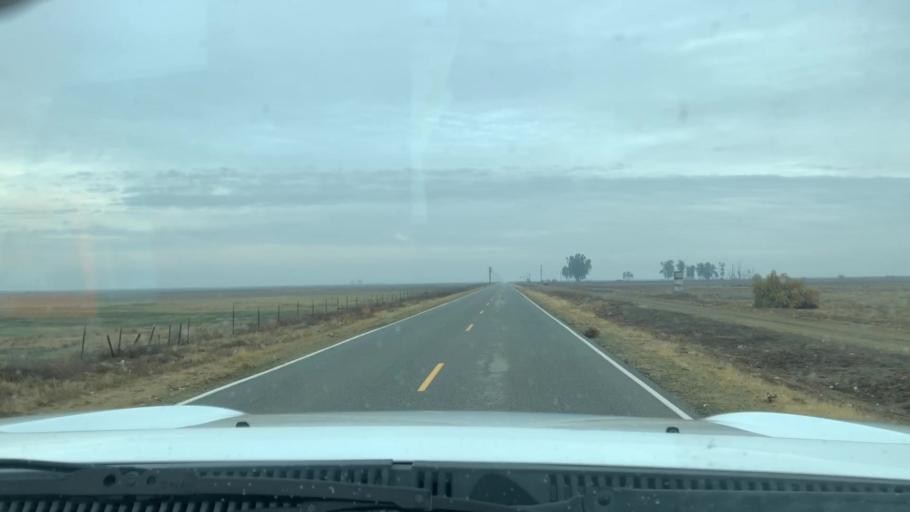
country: US
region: California
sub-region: Kern County
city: Lost Hills
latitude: 35.6620
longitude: -119.5800
